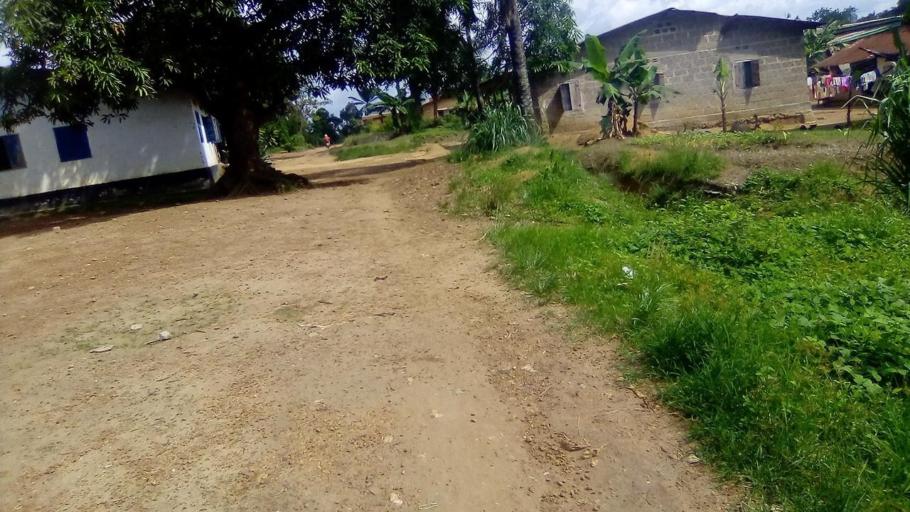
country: SL
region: Southern Province
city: Bo
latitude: 7.9566
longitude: -11.7177
